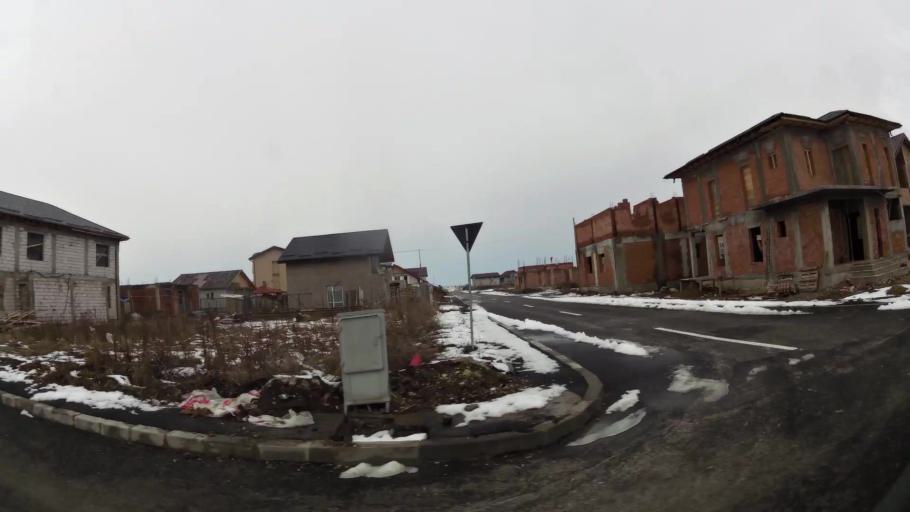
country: RO
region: Ilfov
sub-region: Comuna Tunari
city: Tunari
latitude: 44.5508
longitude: 26.1549
